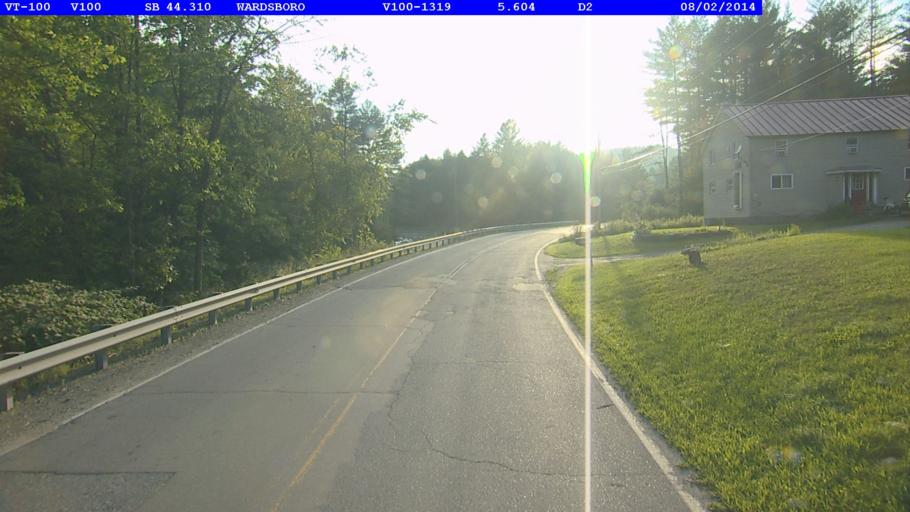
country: US
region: Vermont
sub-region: Windham County
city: Dover
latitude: 43.0338
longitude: -72.8025
